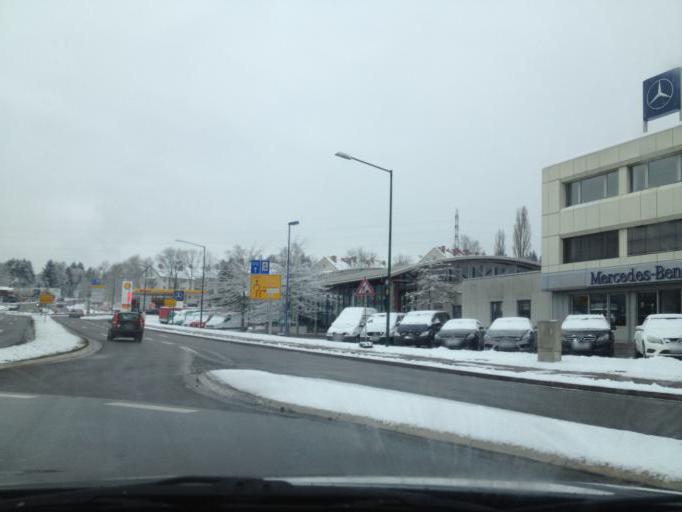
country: DE
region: Saarland
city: Neunkirchen
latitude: 49.3308
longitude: 7.1926
